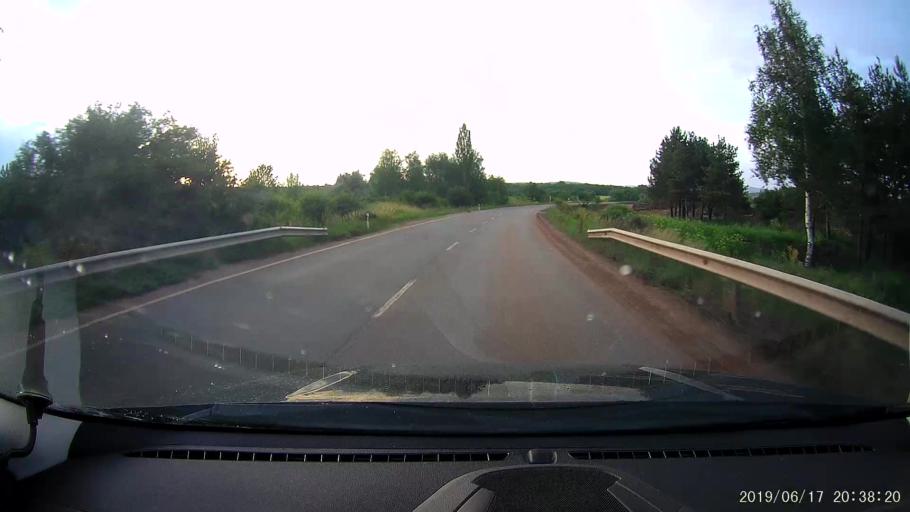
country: BG
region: Sofiya
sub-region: Obshtina Slivnitsa
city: Slivnitsa
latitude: 42.8708
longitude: 23.0192
